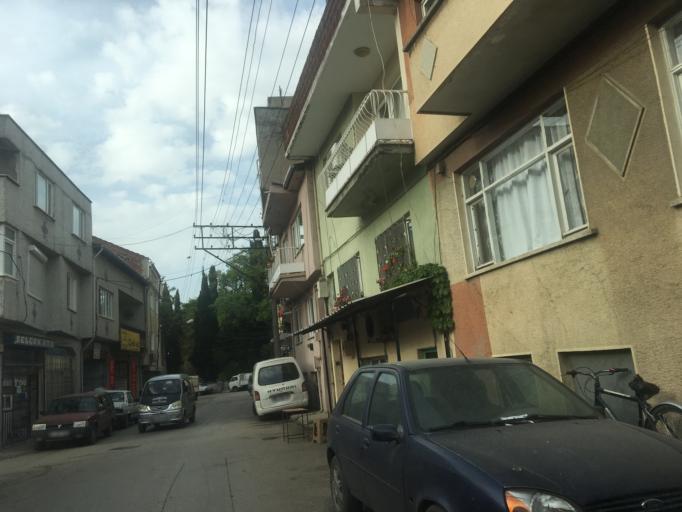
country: TR
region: Bursa
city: Yildirim
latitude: 40.2014
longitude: 29.0457
